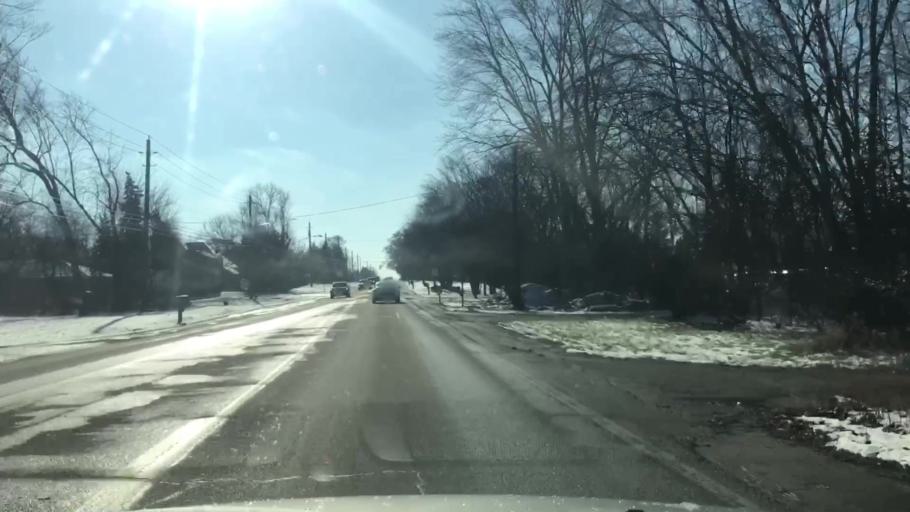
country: US
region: Michigan
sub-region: Oakland County
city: Troy
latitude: 42.6225
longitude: -83.1108
